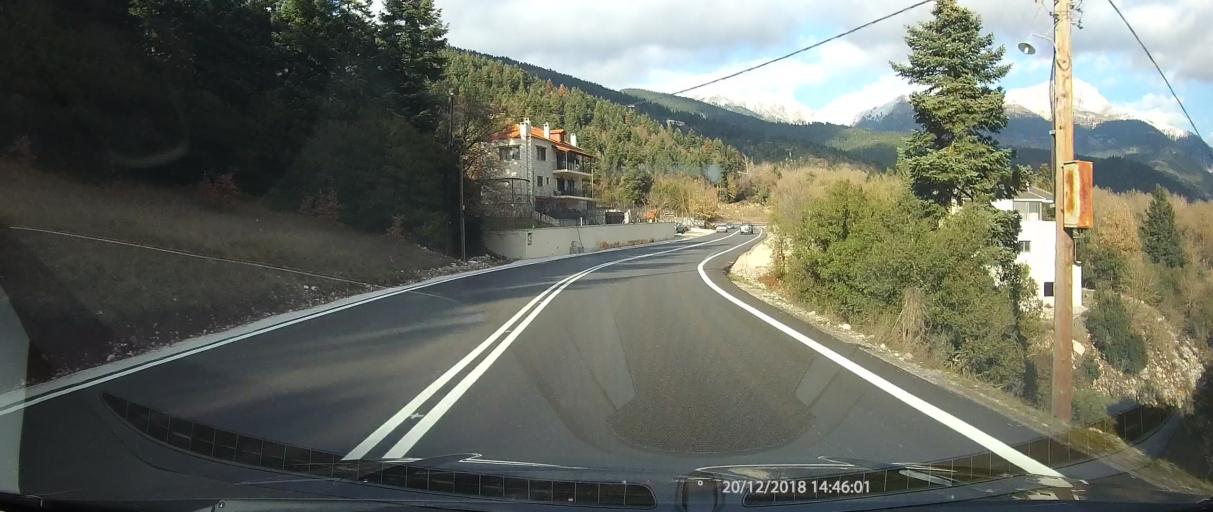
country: GR
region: Central Greece
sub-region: Nomos Evrytanias
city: Karpenisi
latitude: 38.8934
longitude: 21.7643
